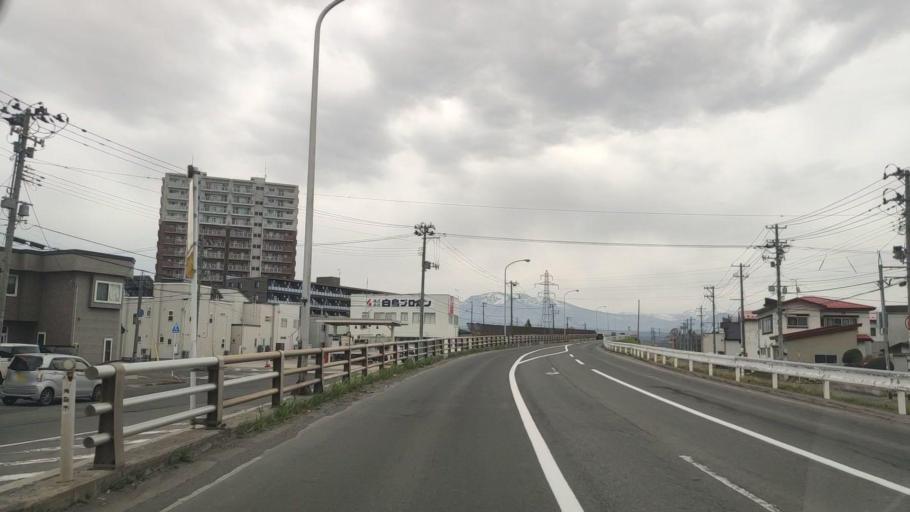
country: JP
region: Aomori
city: Aomori Shi
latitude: 40.8109
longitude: 140.7786
